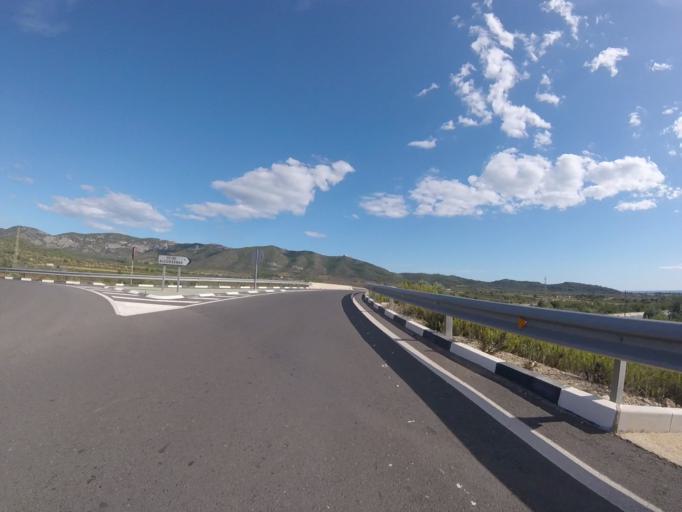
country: ES
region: Valencia
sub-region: Provincia de Castello
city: Alcala de Xivert
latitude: 40.2680
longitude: 0.2400
